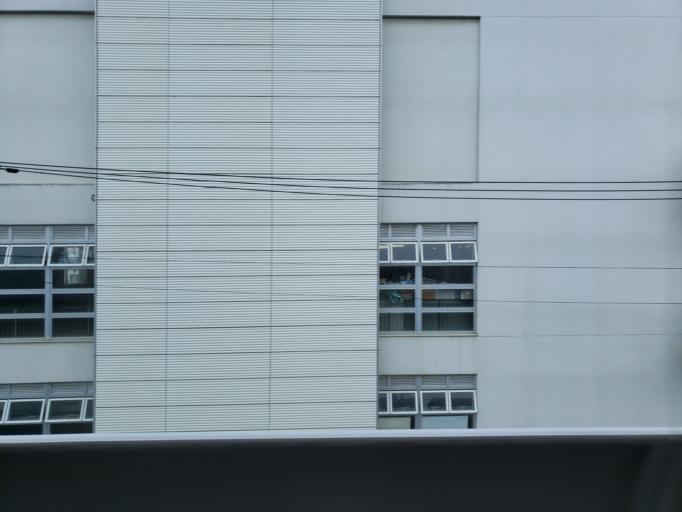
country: JP
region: Hyogo
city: Ashiya
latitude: 34.7240
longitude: 135.2945
